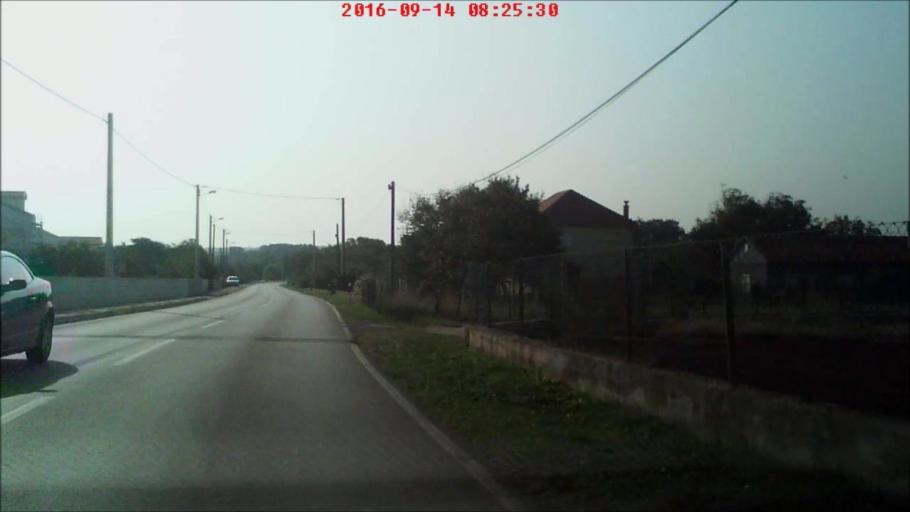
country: HR
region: Zadarska
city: Vrsi
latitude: 44.2029
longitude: 15.2546
